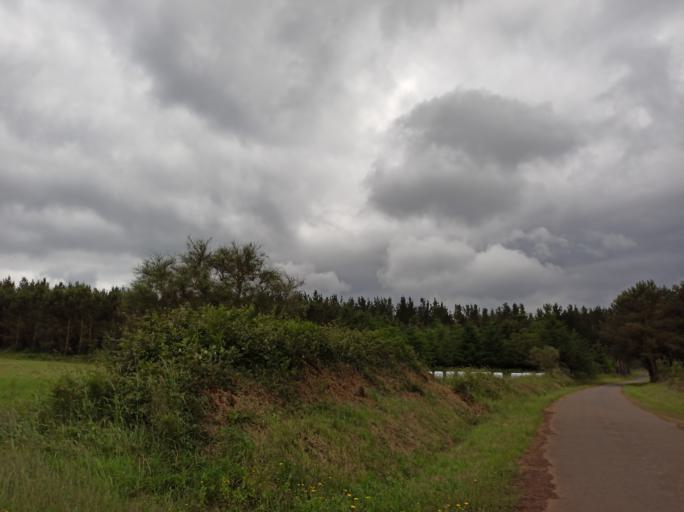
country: ES
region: Galicia
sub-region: Provincia de Pontevedra
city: Silleda
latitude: 42.7650
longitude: -8.1604
